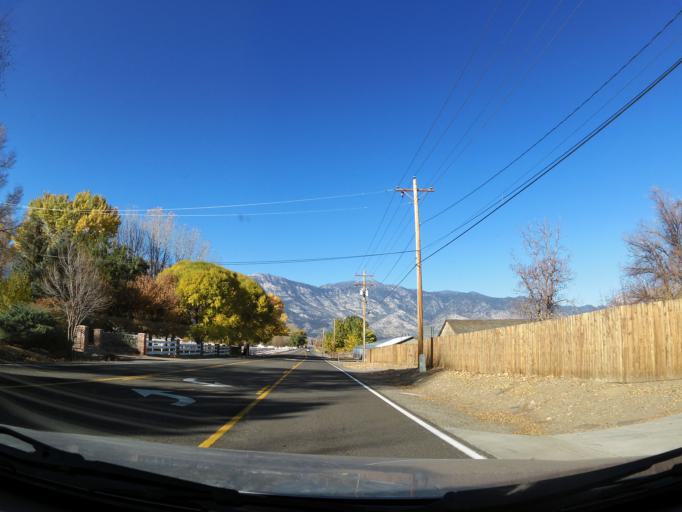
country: US
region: Nevada
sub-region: Douglas County
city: Gardnerville Ranchos
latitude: 38.9107
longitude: -119.7625
